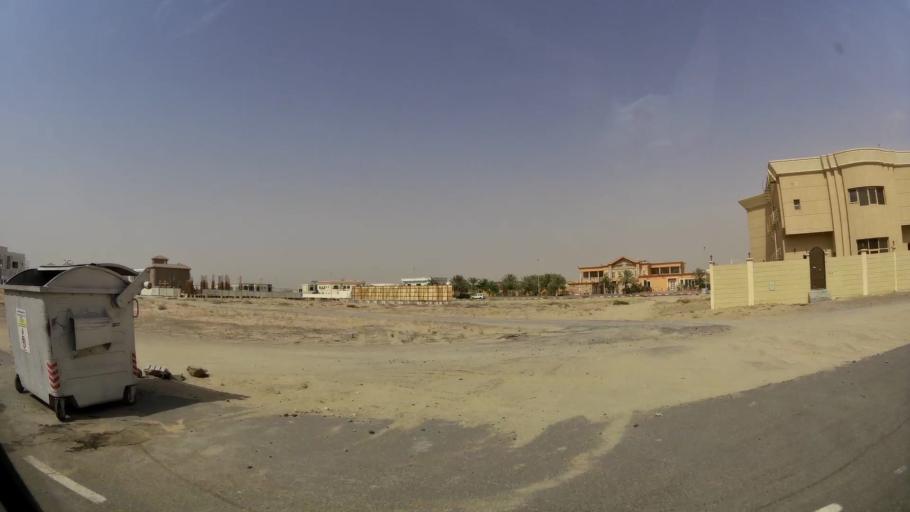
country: AE
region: Ash Shariqah
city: Sharjah
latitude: 25.2587
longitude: 55.4689
